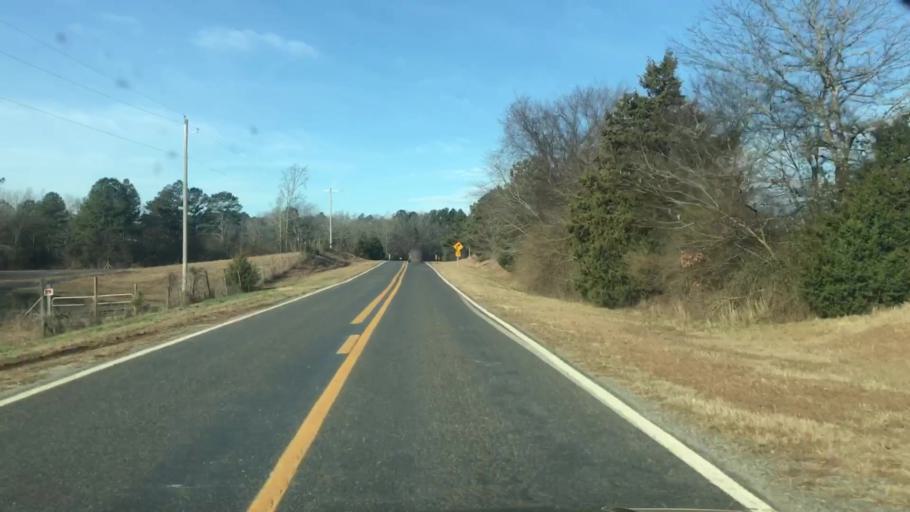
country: US
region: Arkansas
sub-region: Garland County
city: Rockwell
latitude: 34.4713
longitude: -93.2531
